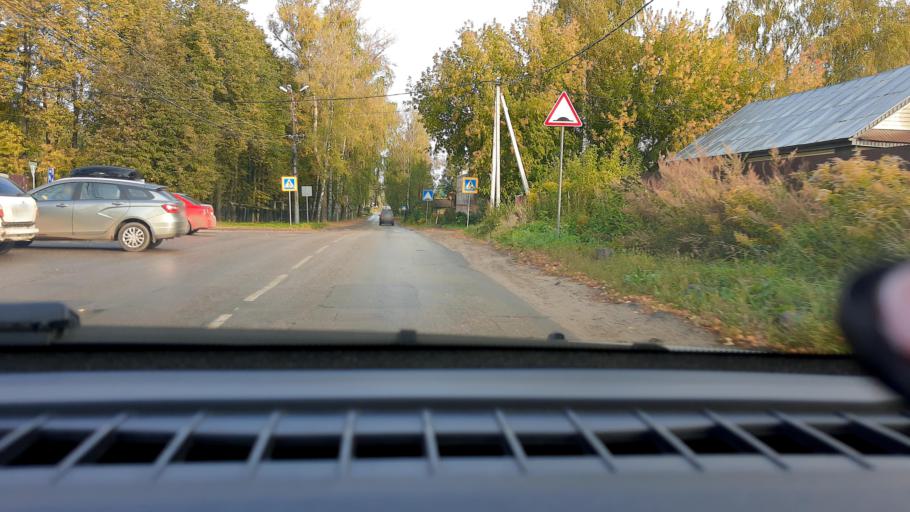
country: RU
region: Nizjnij Novgorod
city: Kstovo
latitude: 56.1839
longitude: 44.1652
